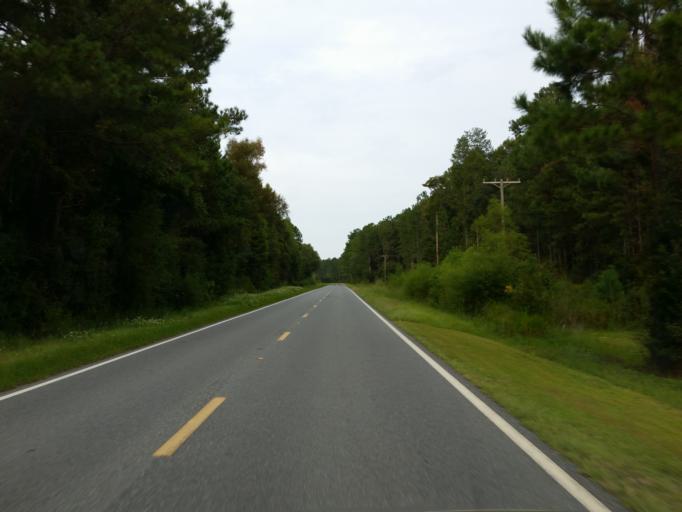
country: US
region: Georgia
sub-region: Echols County
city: Statenville
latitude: 30.5717
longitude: -83.1540
